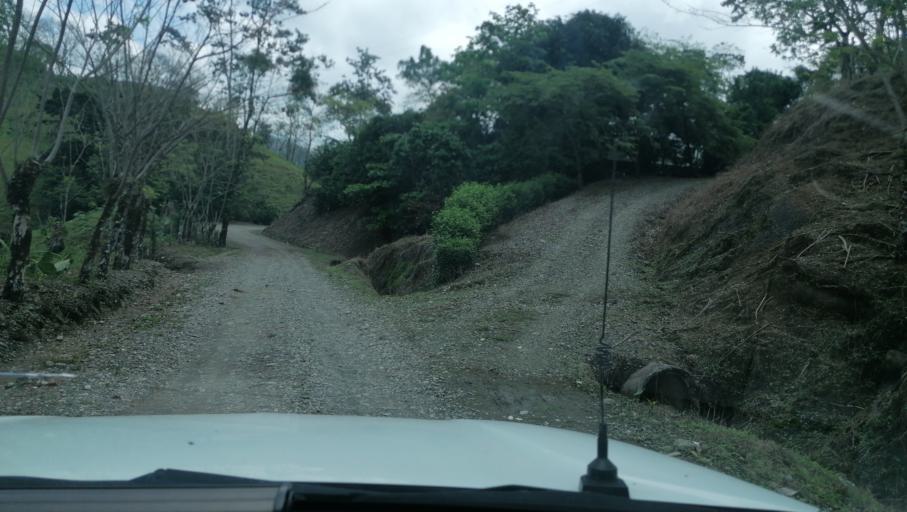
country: MX
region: Chiapas
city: Ixtacomitan
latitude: 17.4423
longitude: -93.1998
